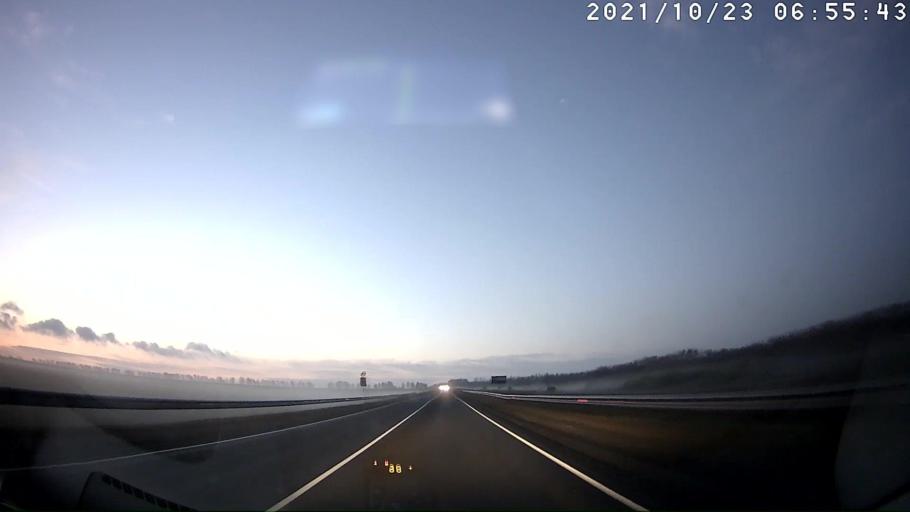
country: RU
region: Saratov
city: Dukhovnitskoye
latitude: 52.7335
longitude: 48.2572
